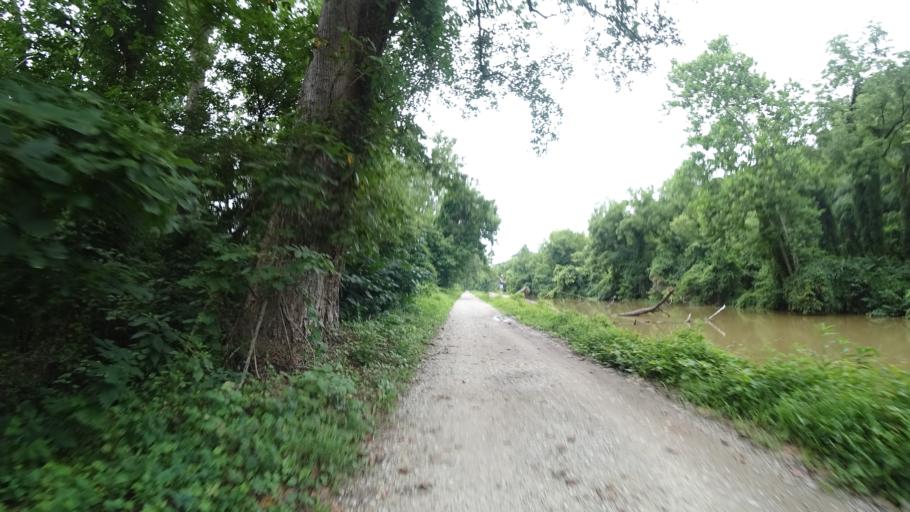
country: US
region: Maryland
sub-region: Montgomery County
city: Brookmont
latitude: 38.9358
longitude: -77.1166
